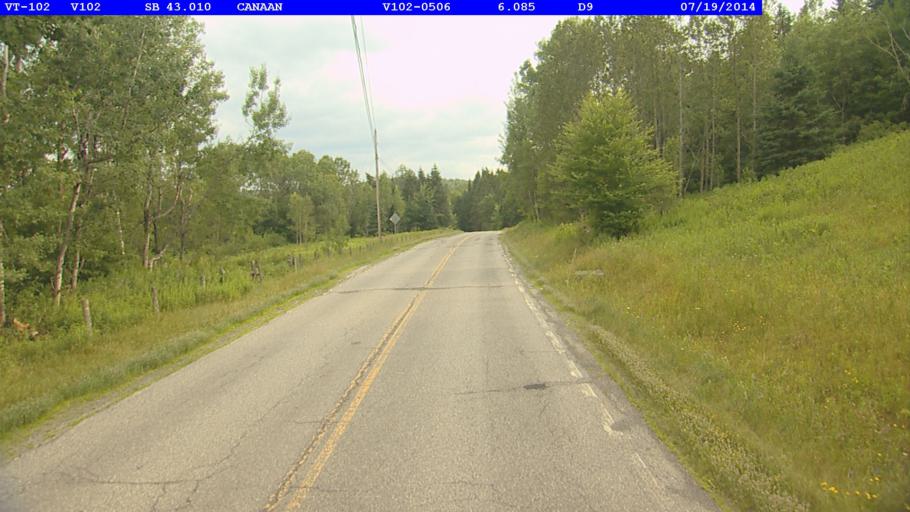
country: US
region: New Hampshire
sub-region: Coos County
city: Colebrook
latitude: 44.9863
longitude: -71.5424
